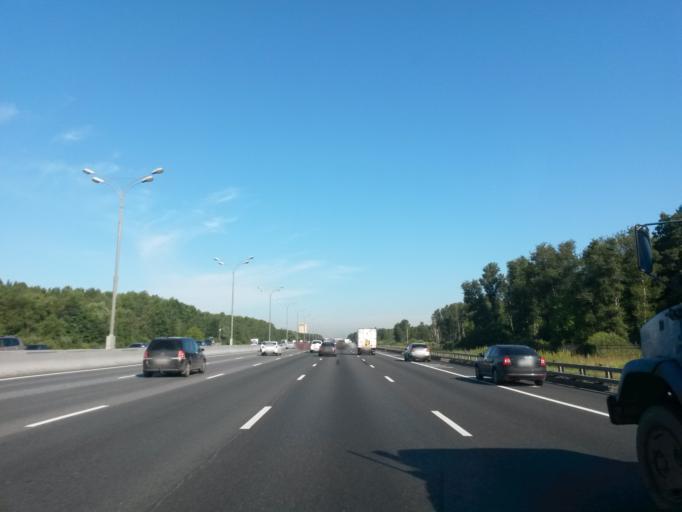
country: RU
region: Moskovskaya
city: Druzhba
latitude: 55.8663
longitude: 37.7577
